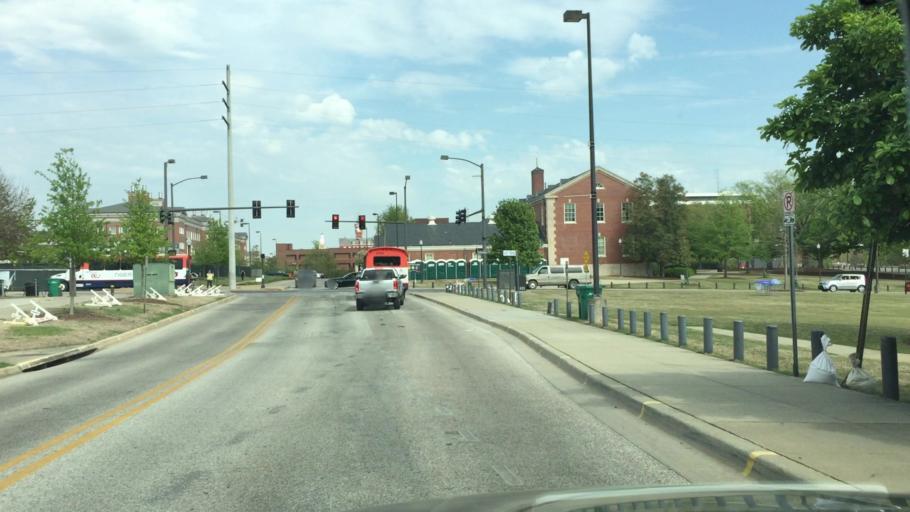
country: US
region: Alabama
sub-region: Lee County
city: Auburn
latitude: 32.6048
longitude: -85.4912
